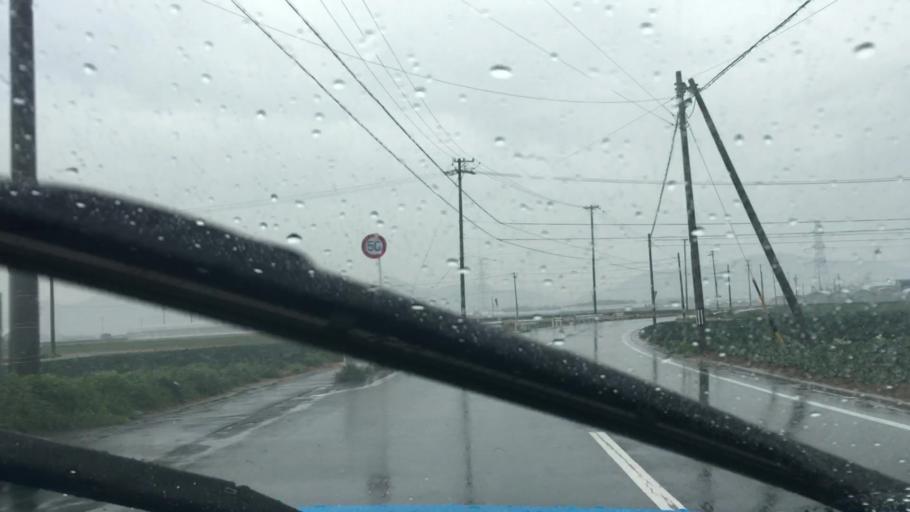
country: JP
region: Aichi
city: Tahara
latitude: 34.6490
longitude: 137.2929
